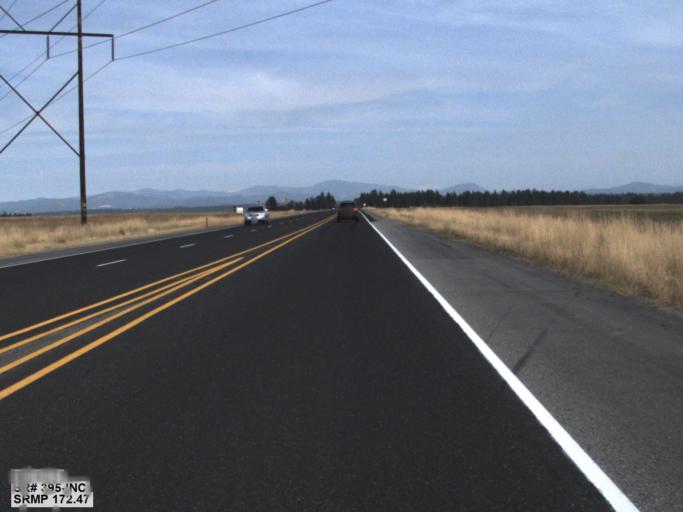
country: US
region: Washington
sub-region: Spokane County
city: Fairwood
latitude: 47.8510
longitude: -117.4218
